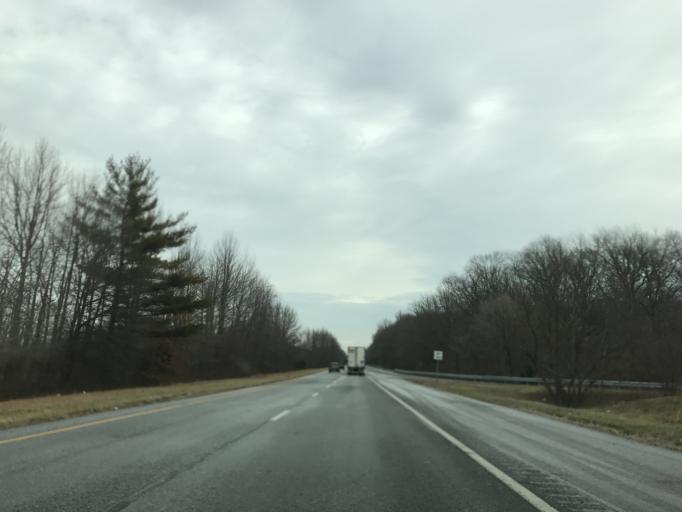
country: US
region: New Jersey
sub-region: Salem County
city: Carneys Point
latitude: 39.7100
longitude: -75.4436
